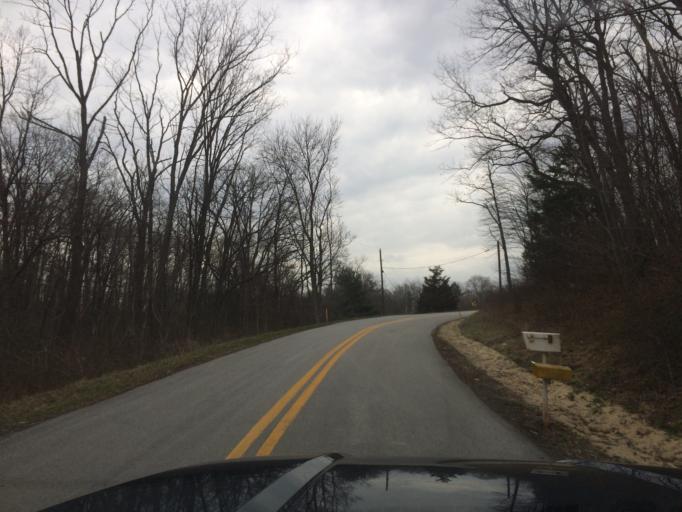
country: US
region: Maryland
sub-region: Carroll County
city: New Windsor
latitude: 39.5346
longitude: -77.1436
